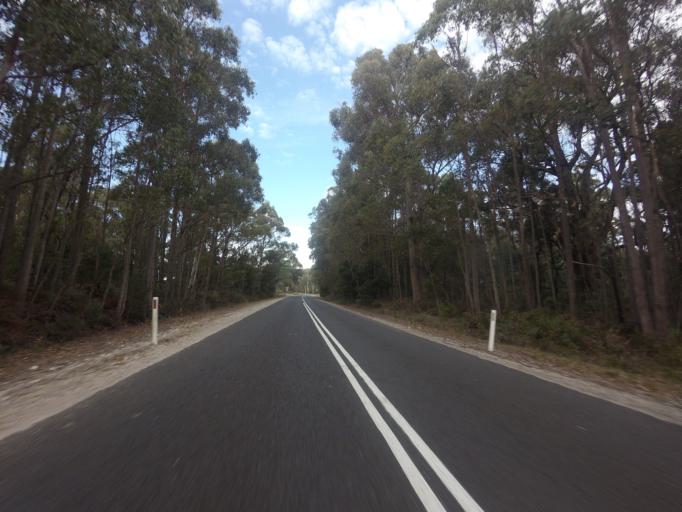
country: AU
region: Tasmania
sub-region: Meander Valley
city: Deloraine
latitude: -41.6157
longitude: 146.6910
